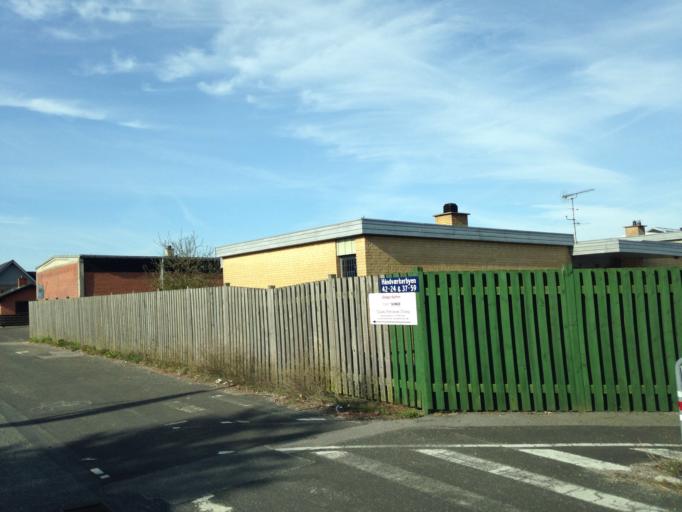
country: DK
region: Zealand
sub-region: Greve Kommune
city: Greve
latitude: 55.5910
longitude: 12.2962
